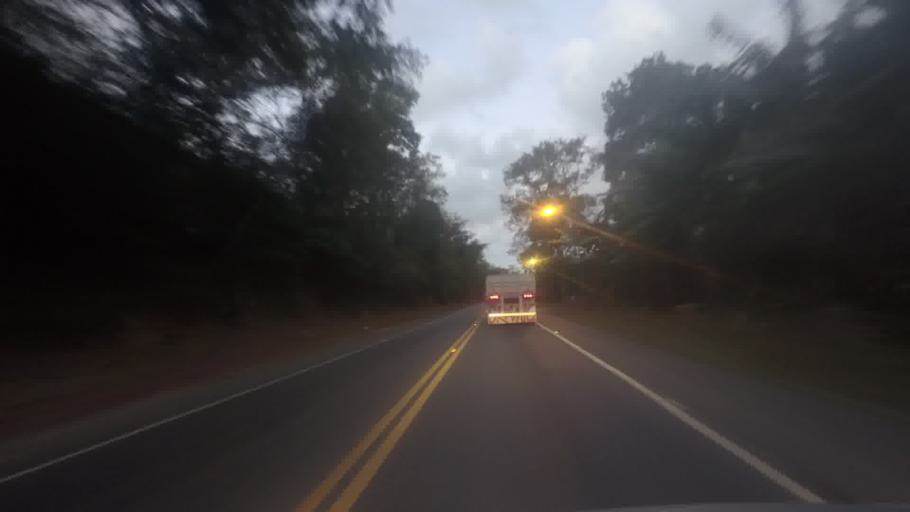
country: BR
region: Espirito Santo
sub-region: Iconha
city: Iconha
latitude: -20.7972
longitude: -40.8213
